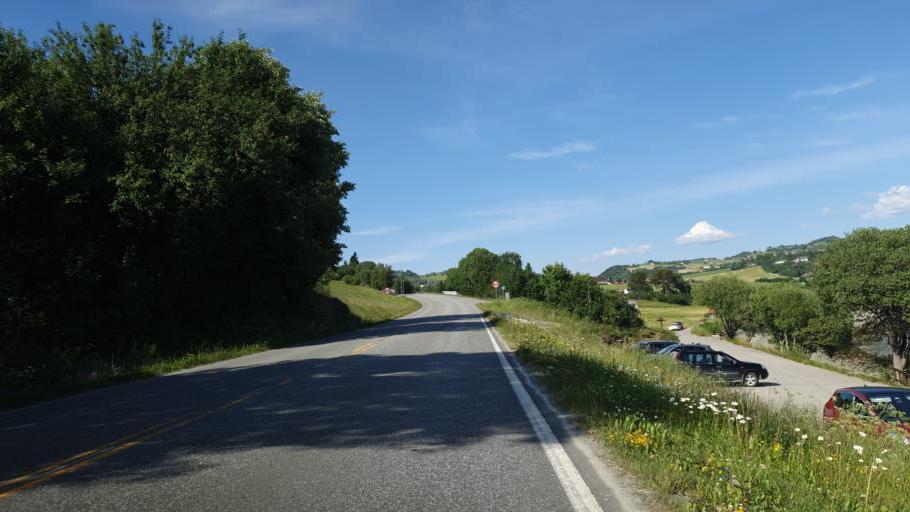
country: NO
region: Nord-Trondelag
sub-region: Leksvik
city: Leksvik
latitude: 63.6624
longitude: 10.6081
